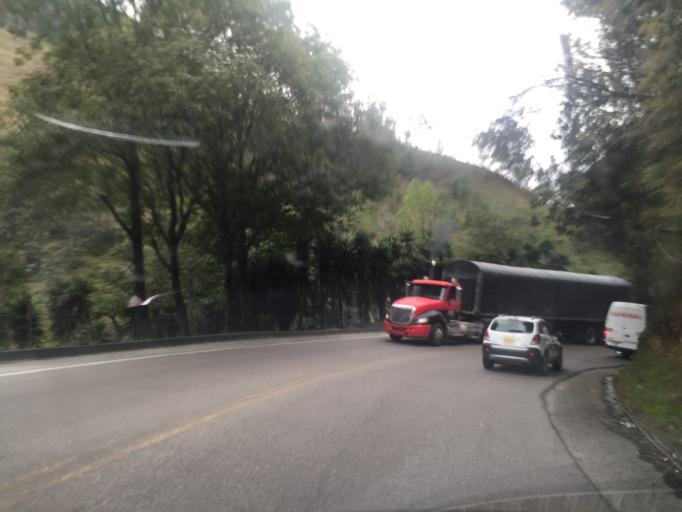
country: CO
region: Tolima
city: Cajamarca
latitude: 4.4342
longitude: -75.4575
